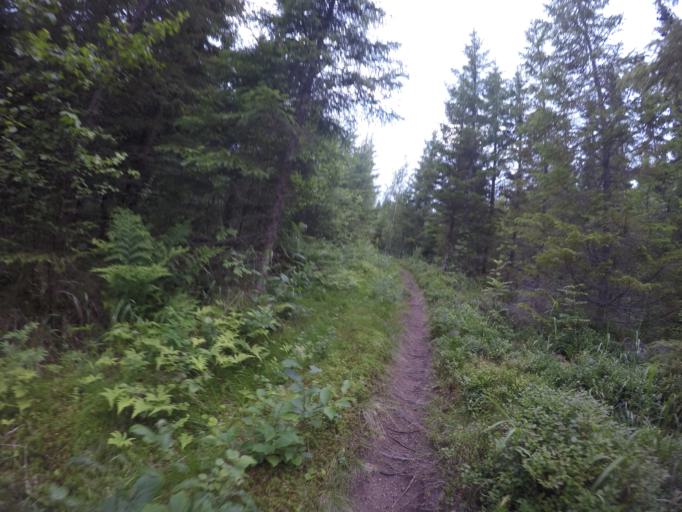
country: SE
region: Vaermland
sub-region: Filipstads Kommun
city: Lesjofors
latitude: 60.1578
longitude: 14.3951
